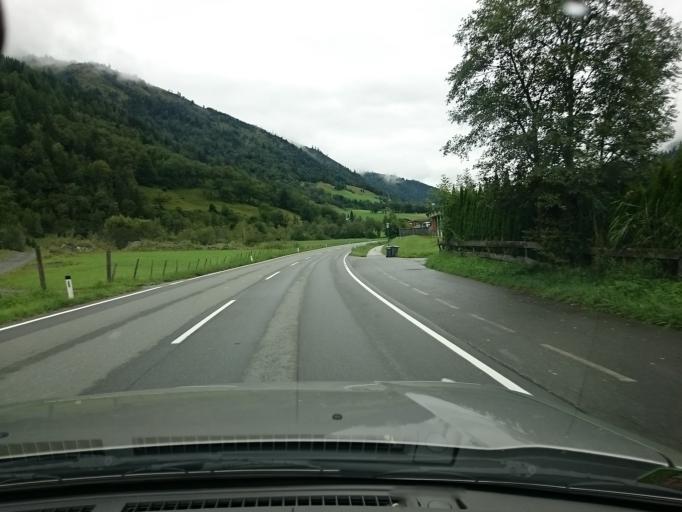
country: AT
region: Salzburg
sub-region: Politischer Bezirk Zell am See
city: Bruck an der Grossglocknerstrasse
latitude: 47.2375
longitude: 12.8249
